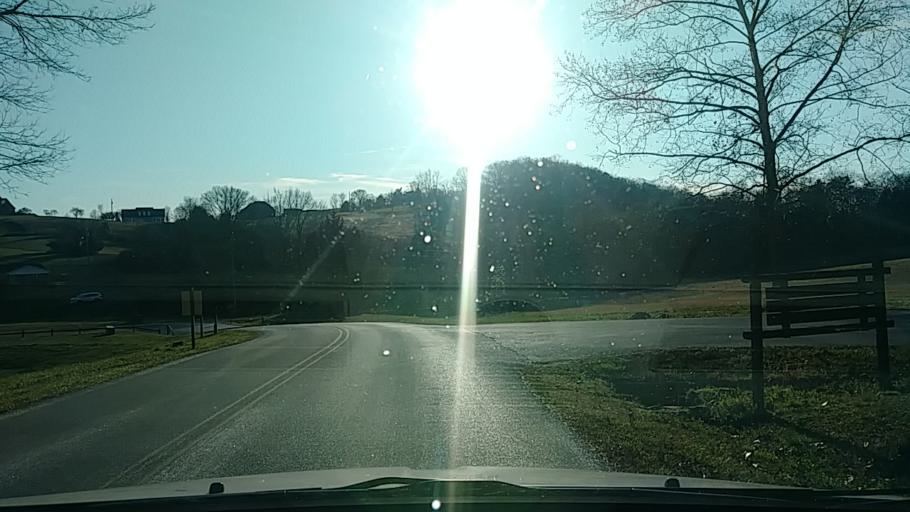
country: US
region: Tennessee
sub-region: Hamblen County
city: Morristown
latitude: 36.2062
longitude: -83.4067
